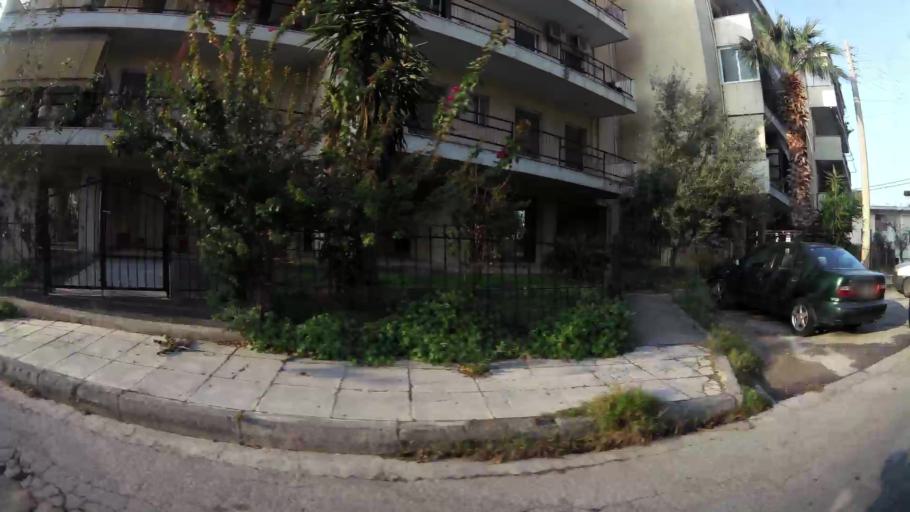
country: GR
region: Attica
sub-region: Nomarchia Dytikis Attikis
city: Zefyri
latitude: 38.0550
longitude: 23.7215
